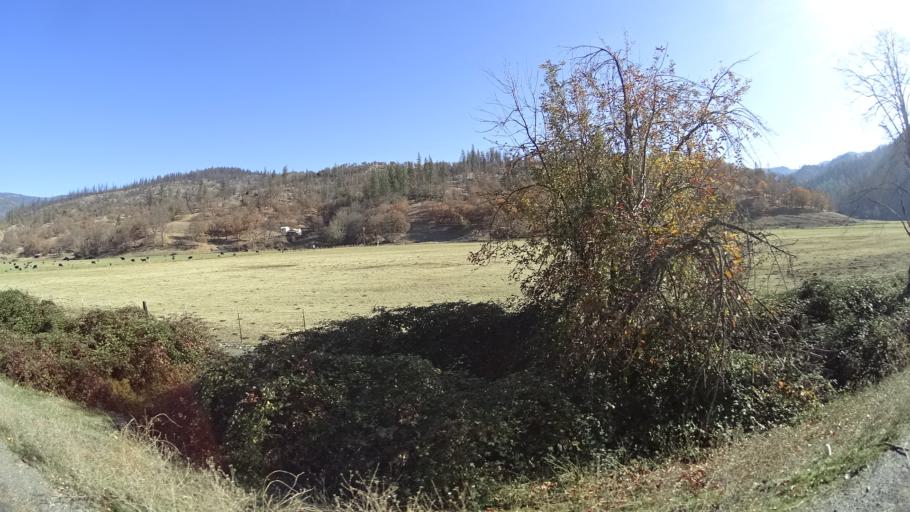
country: US
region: California
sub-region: Siskiyou County
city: Happy Camp
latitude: 41.8276
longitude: -123.0058
